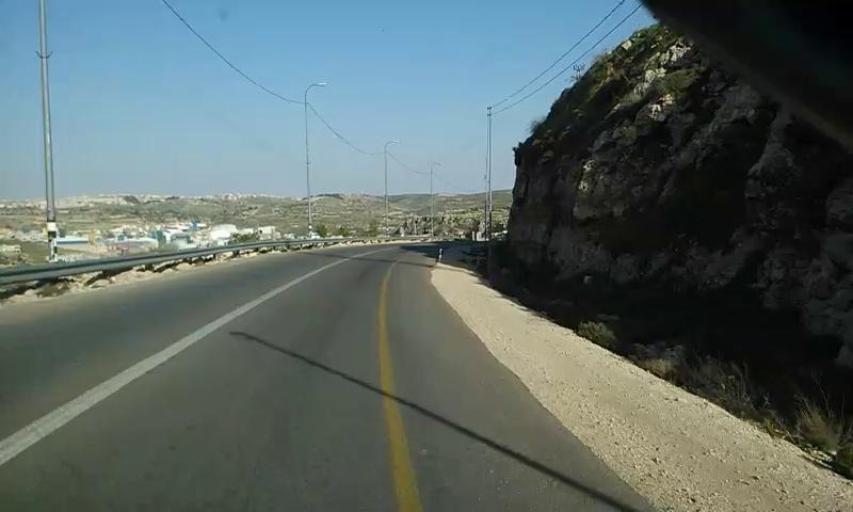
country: PS
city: Khallat ad Dar
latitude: 31.5024
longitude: 35.1103
